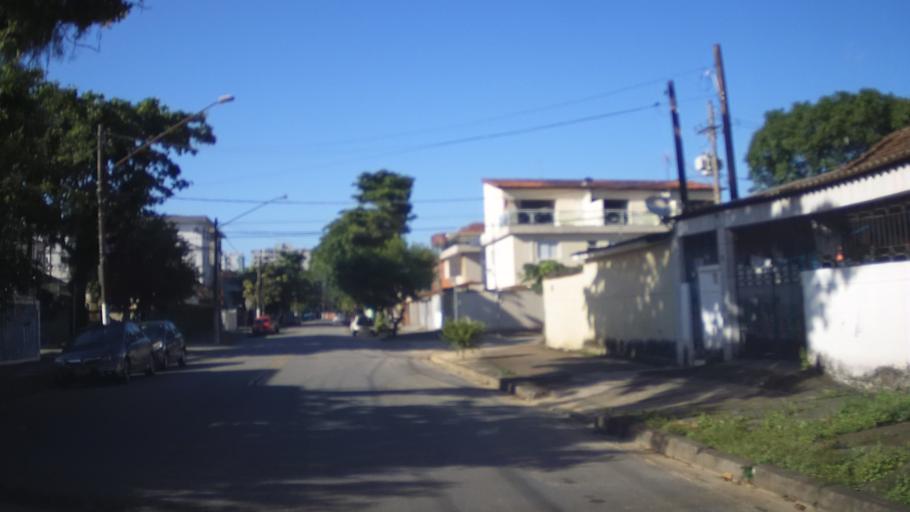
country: BR
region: Sao Paulo
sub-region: Santos
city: Santos
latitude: -23.9485
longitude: -46.3424
